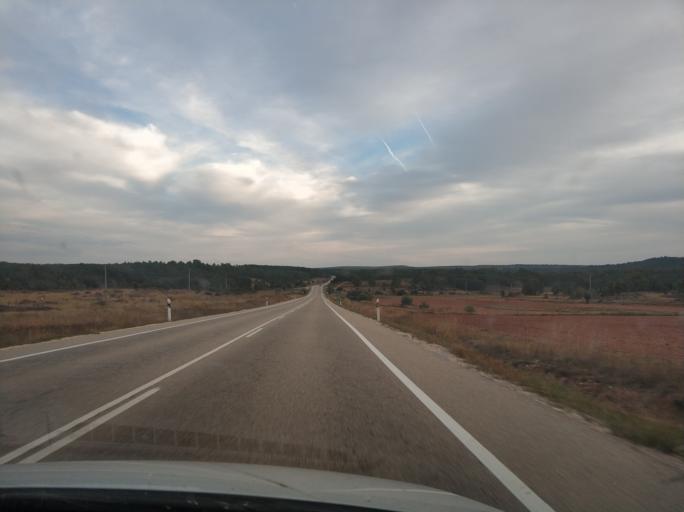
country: ES
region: Castille and Leon
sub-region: Provincia de Burgos
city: Hacinas
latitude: 41.9598
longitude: -3.2914
